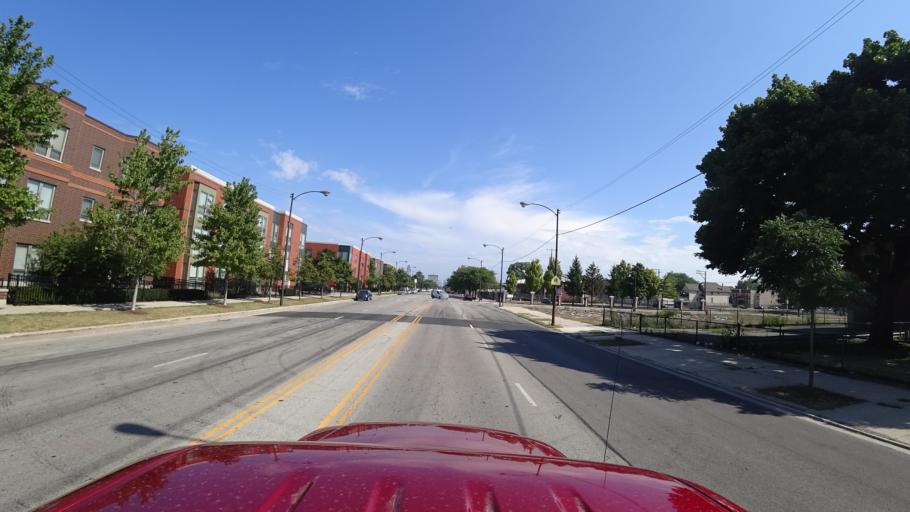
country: US
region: Illinois
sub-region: Cook County
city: Chicago
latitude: 41.8140
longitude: -87.6262
